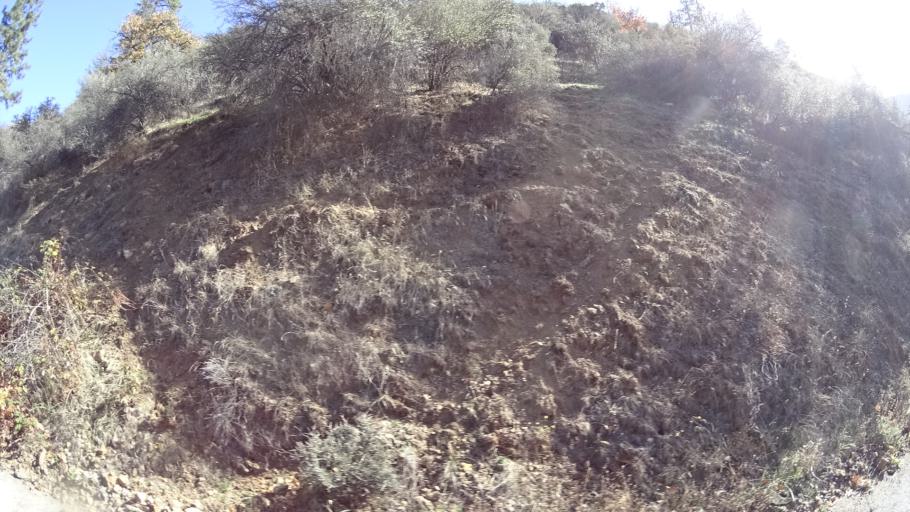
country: US
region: California
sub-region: Siskiyou County
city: Yreka
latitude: 41.8327
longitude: -122.6384
